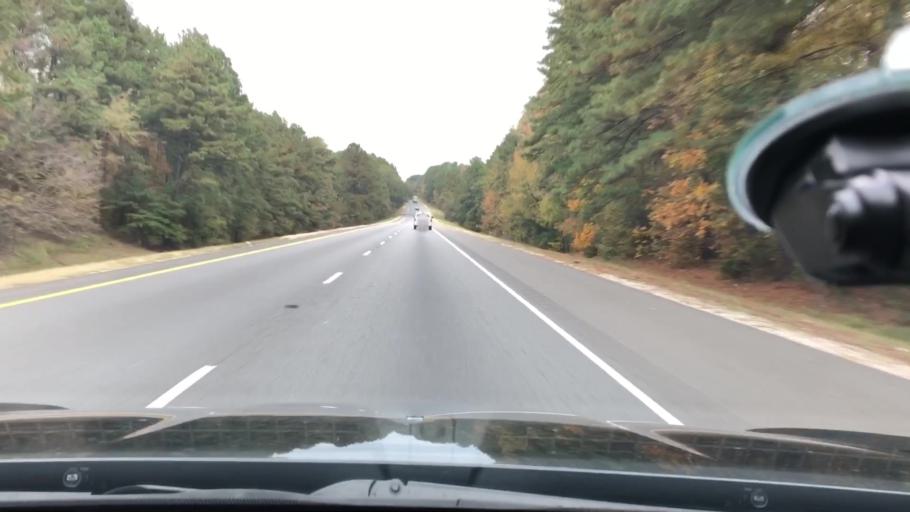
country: US
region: Arkansas
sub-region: Hot Spring County
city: Malvern
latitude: 34.3043
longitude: -92.9428
